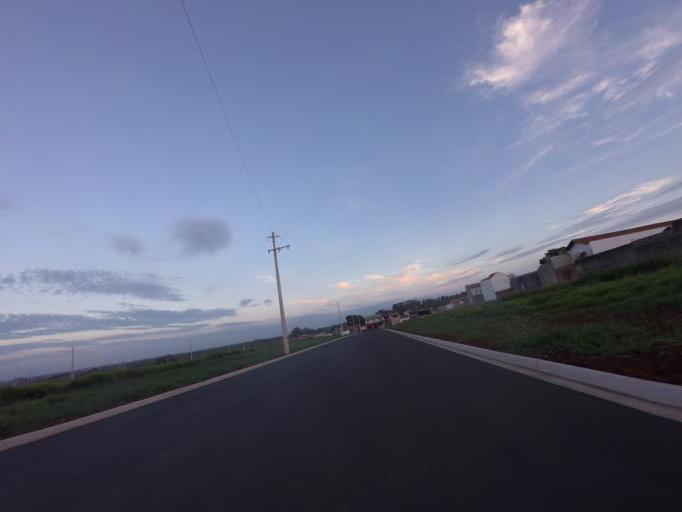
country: BR
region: Sao Paulo
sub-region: Piracicaba
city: Piracicaba
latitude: -22.7657
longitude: -47.5872
